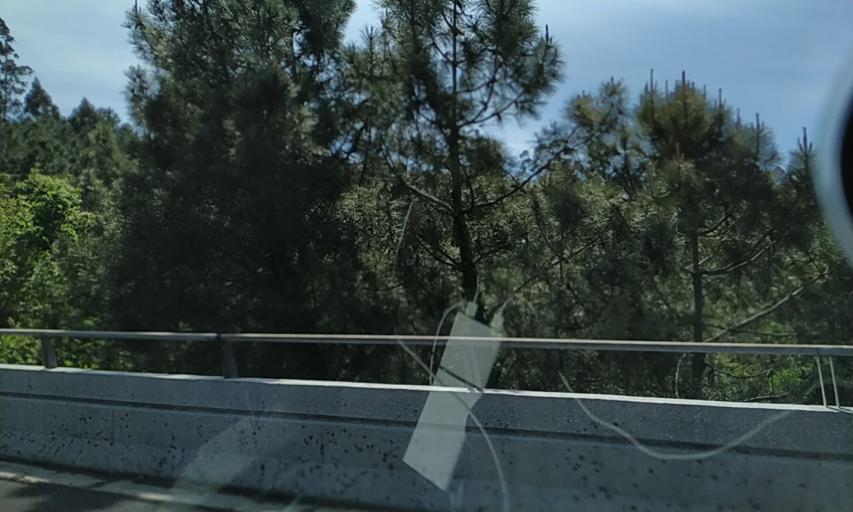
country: ES
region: Galicia
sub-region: Provincia de Pontevedra
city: Valga
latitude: 42.6762
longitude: -8.6328
